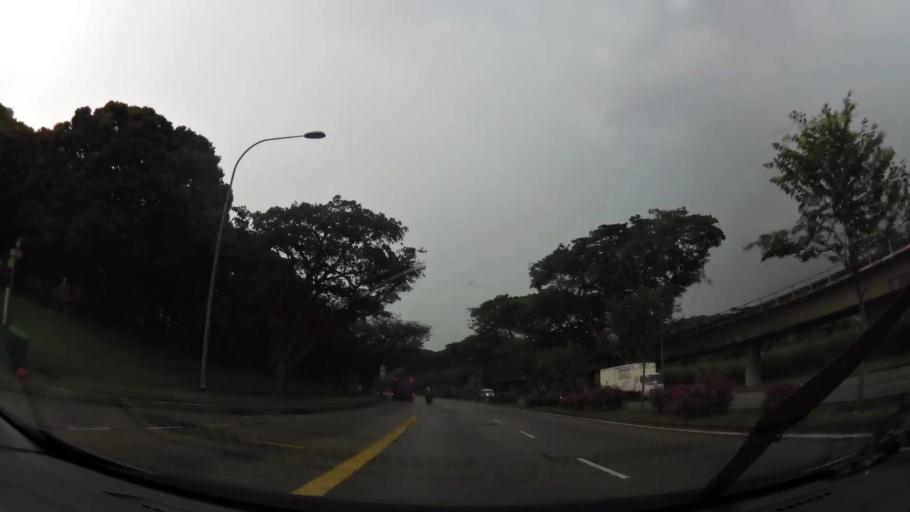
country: MY
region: Johor
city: Kampung Pasir Gudang Baru
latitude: 1.3895
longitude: 103.8407
